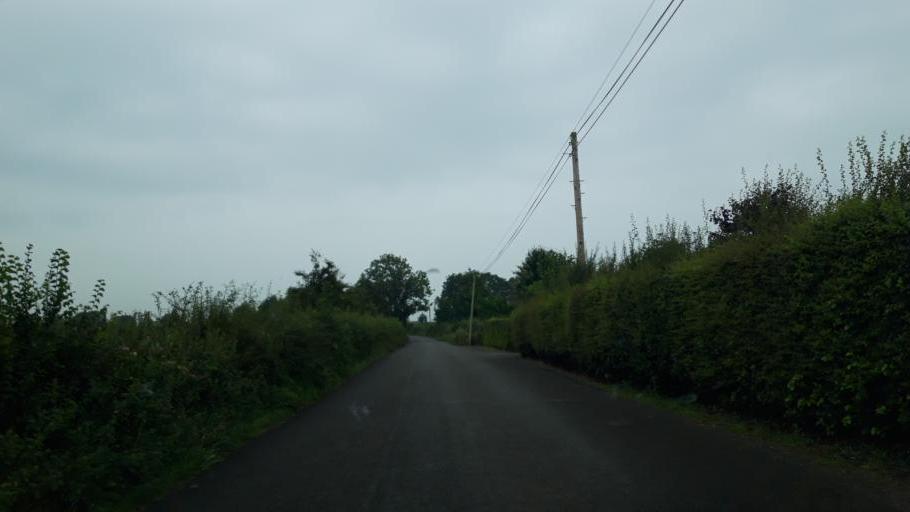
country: IE
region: Leinster
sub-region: Kilkenny
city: Thomastown
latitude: 52.6206
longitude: -7.0894
